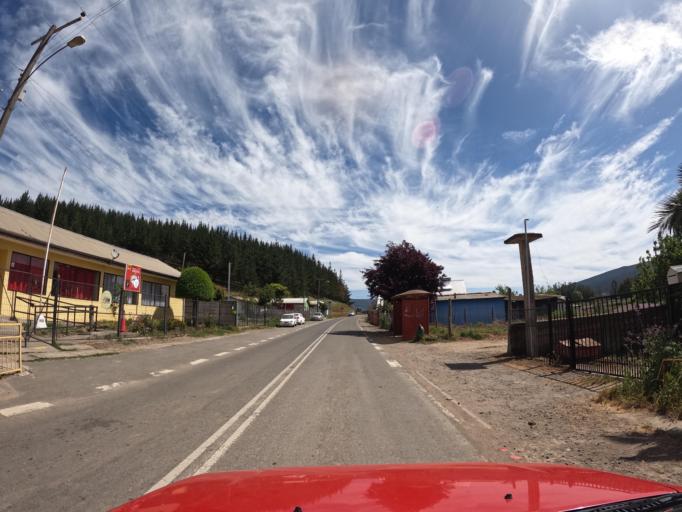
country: CL
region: Maule
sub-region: Provincia de Talca
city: Constitucion
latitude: -35.0231
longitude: -72.0420
